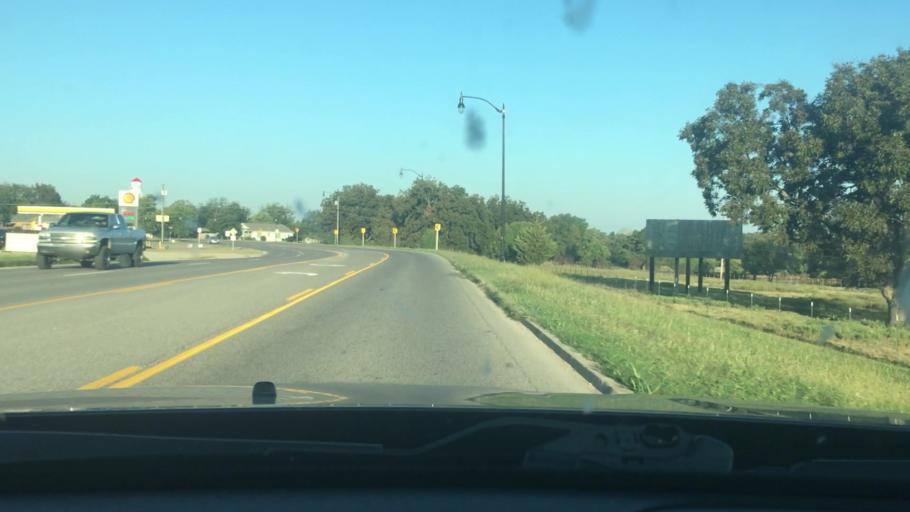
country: US
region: Oklahoma
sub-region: Murray County
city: Davis
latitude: 34.5069
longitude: -97.1090
